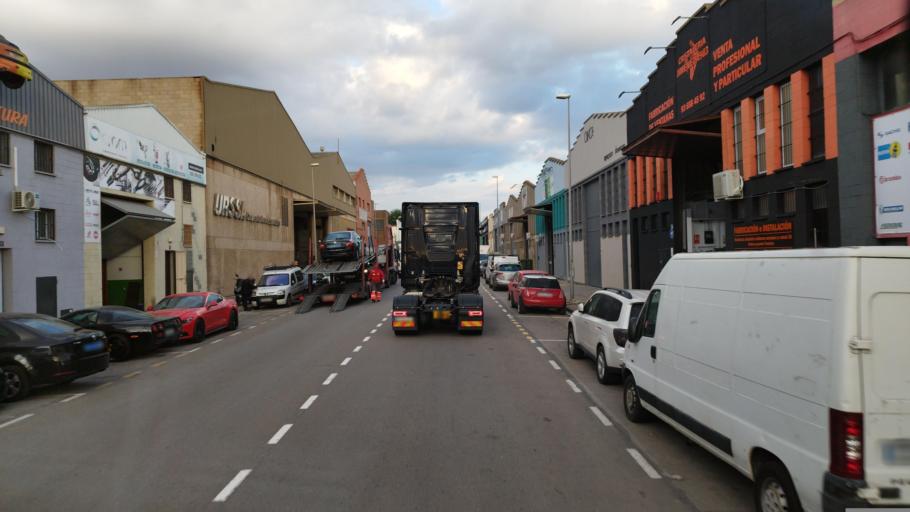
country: ES
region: Catalonia
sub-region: Provincia de Barcelona
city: Viladecans
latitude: 41.3117
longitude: 2.0206
